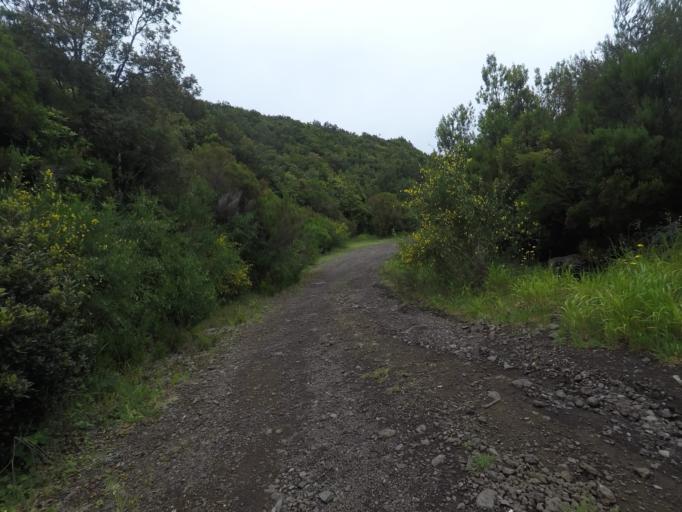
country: PT
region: Madeira
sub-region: Sao Vicente
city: Sao Vicente
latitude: 32.7739
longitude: -17.0557
